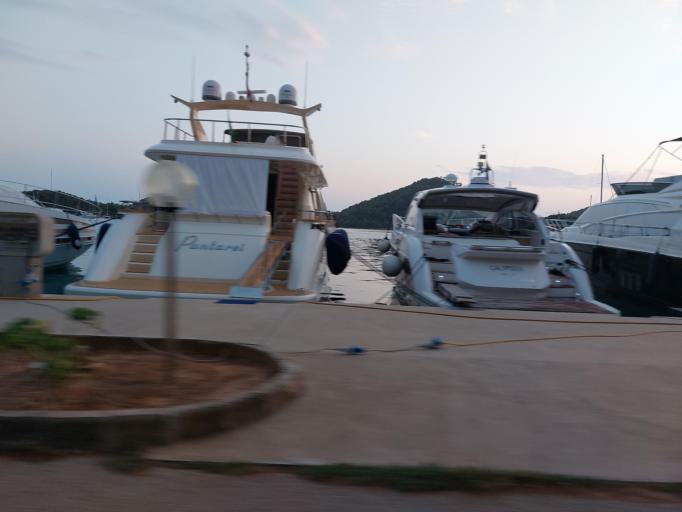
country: HR
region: Dubrovacko-Neretvanska
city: Smokvica
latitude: 42.7651
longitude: 16.8230
